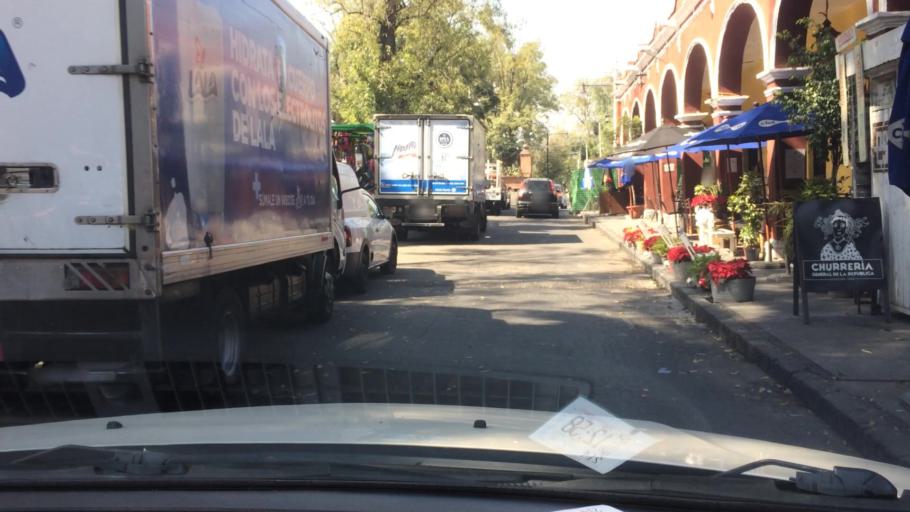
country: MX
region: Mexico City
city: Tlalpan
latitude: 19.2890
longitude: -99.1666
